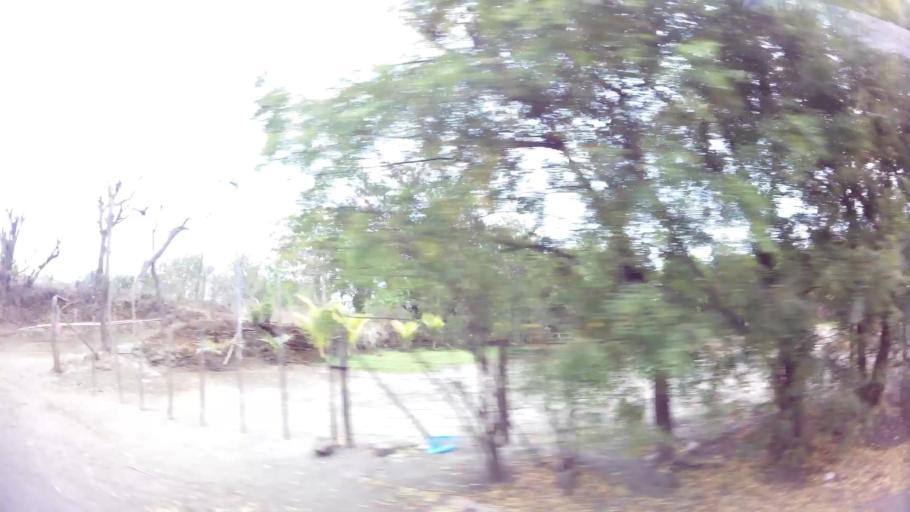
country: NI
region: Masaya
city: Ticuantepe
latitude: 12.0790
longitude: -86.1878
